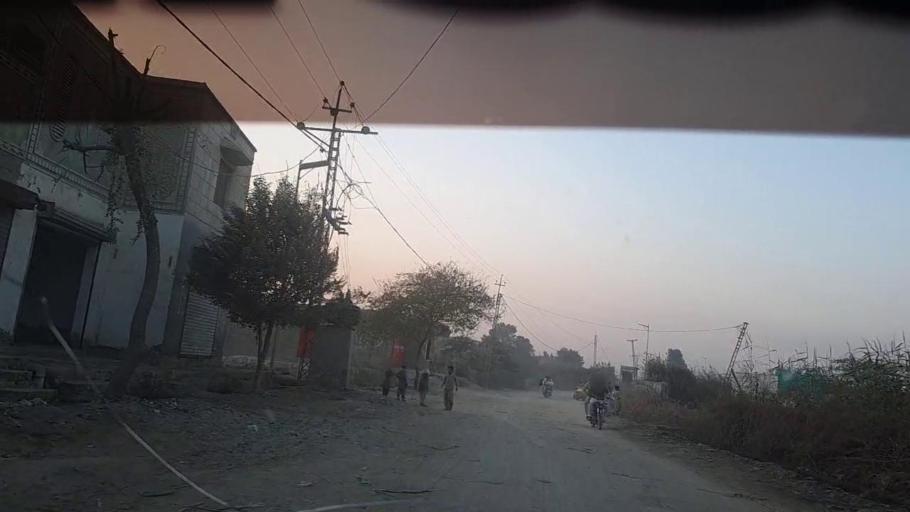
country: PK
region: Sindh
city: Ranipur
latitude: 27.2817
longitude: 68.5152
